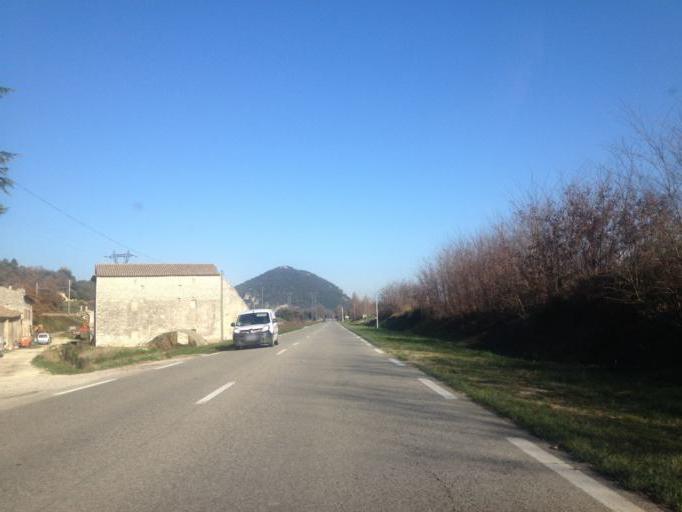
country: FR
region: Rhone-Alpes
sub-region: Departement de l'Ardeche
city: Viviers
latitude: 44.4563
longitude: 4.6864
